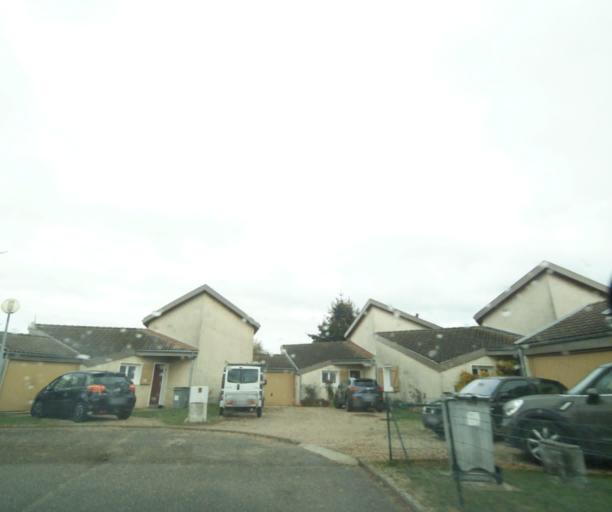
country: FR
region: Rhone-Alpes
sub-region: Departement de l'Ain
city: Loyettes
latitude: 45.7772
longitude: 5.2118
